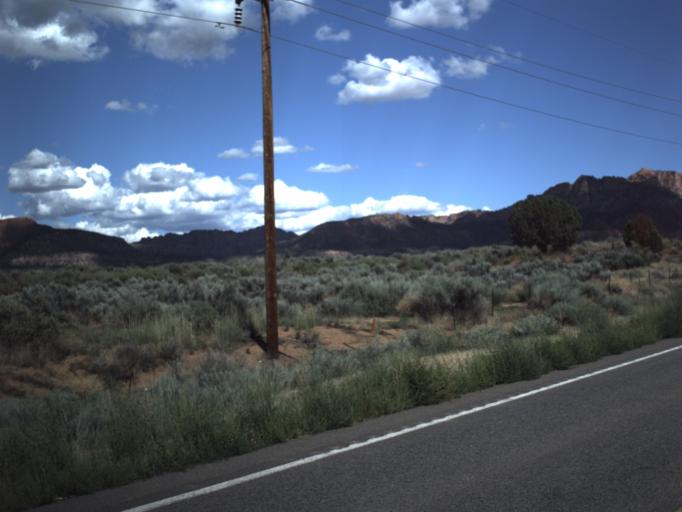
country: US
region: Arizona
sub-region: Mohave County
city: Colorado City
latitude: 37.0944
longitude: -113.1186
